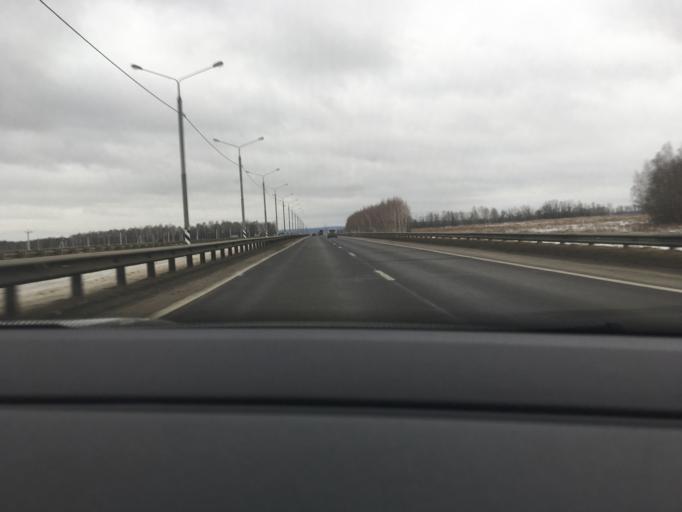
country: RU
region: Tula
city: Zaokskiy
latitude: 54.7997
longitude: 37.4849
